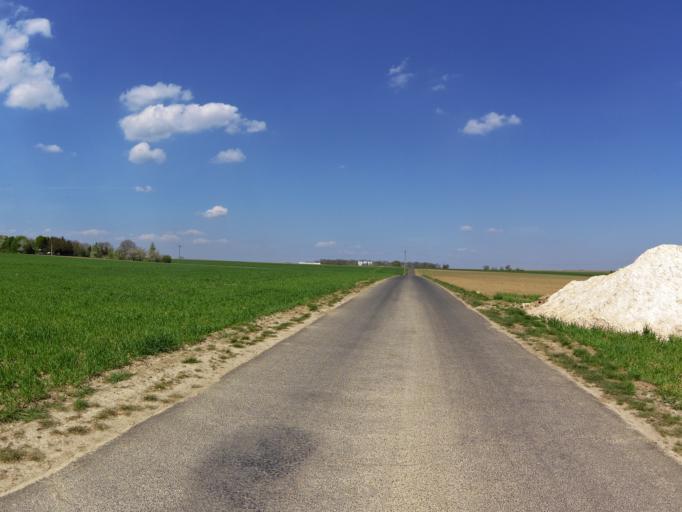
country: DE
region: Bavaria
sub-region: Regierungsbezirk Unterfranken
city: Giebelstadt
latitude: 49.6736
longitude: 9.9519
